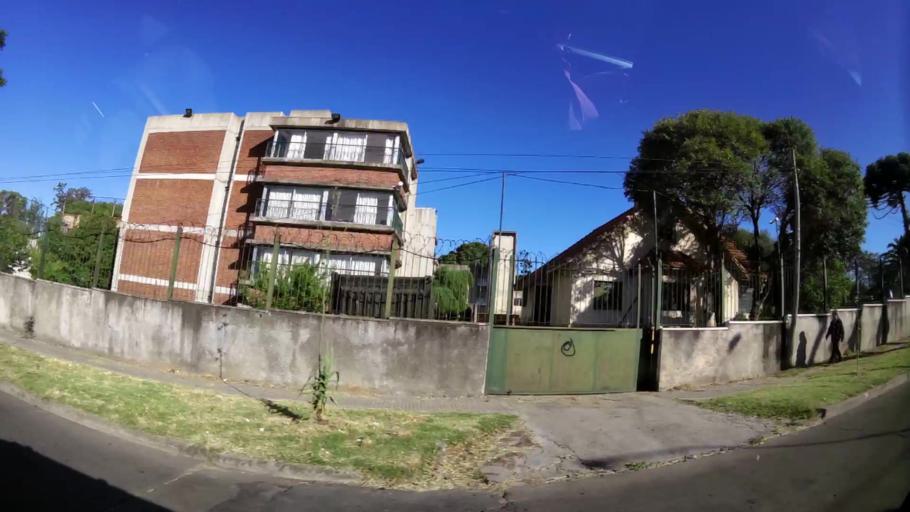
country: UY
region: Montevideo
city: Montevideo
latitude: -34.8434
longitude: -56.2016
